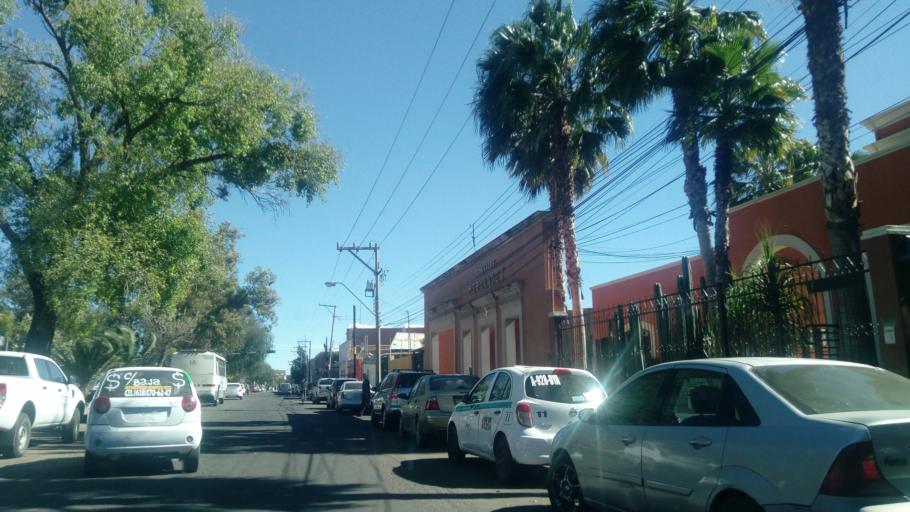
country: MX
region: Durango
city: Victoria de Durango
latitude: 24.0201
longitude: -104.6703
